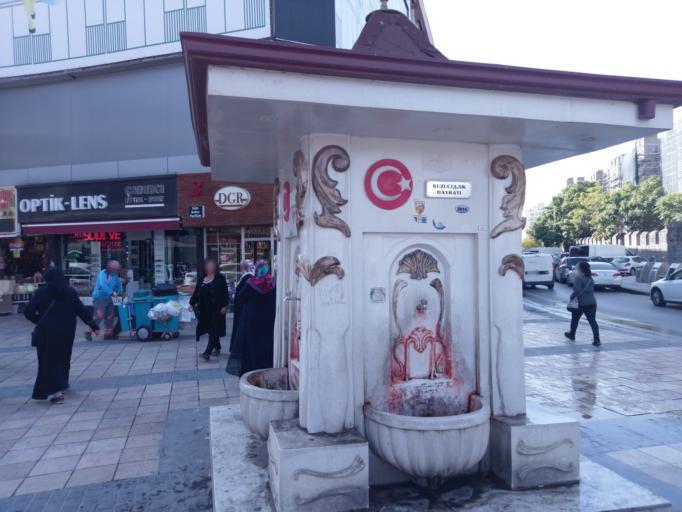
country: TR
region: Kayseri
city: Kayseri
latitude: 38.7205
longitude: 35.4901
